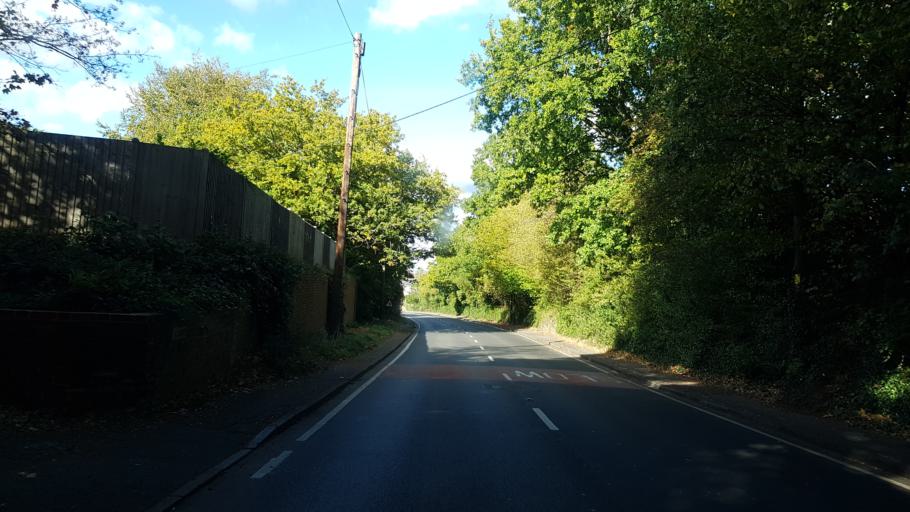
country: GB
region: England
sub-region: Surrey
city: Milford
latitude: 51.1522
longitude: -0.6472
